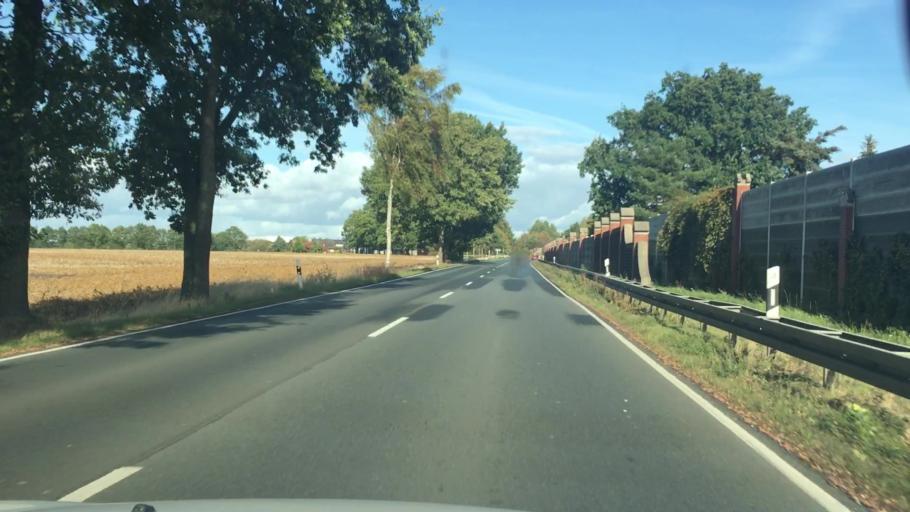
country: DE
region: Lower Saxony
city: Sulingen
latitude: 52.6659
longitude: 8.7765
